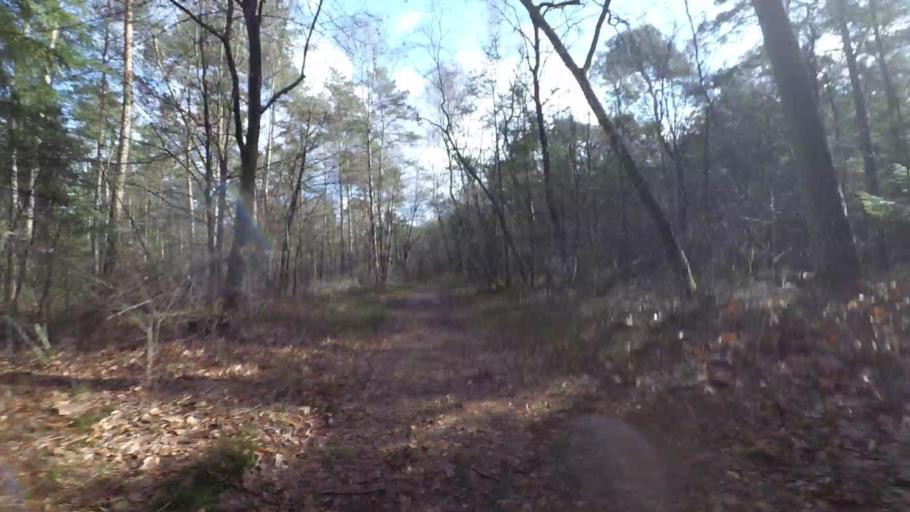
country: NL
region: Utrecht
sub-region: Gemeente Utrechtse Heuvelrug
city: Driebergen-Rijsenburg
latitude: 52.0887
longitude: 5.3141
